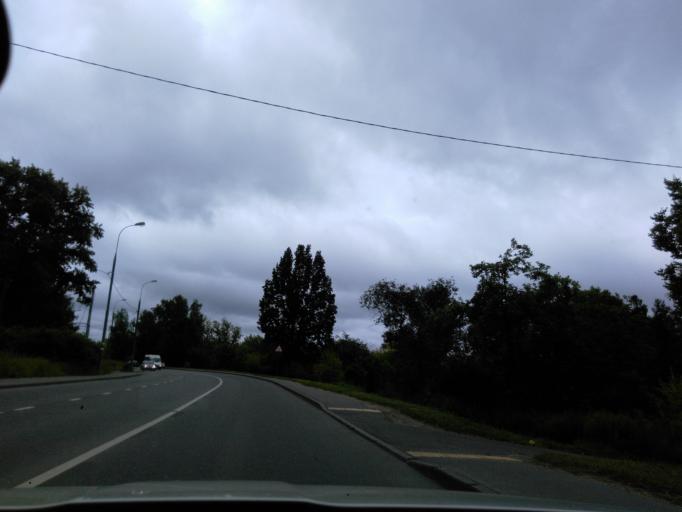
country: RU
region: Moscow
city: Zelenograd
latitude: 55.9727
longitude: 37.1825
